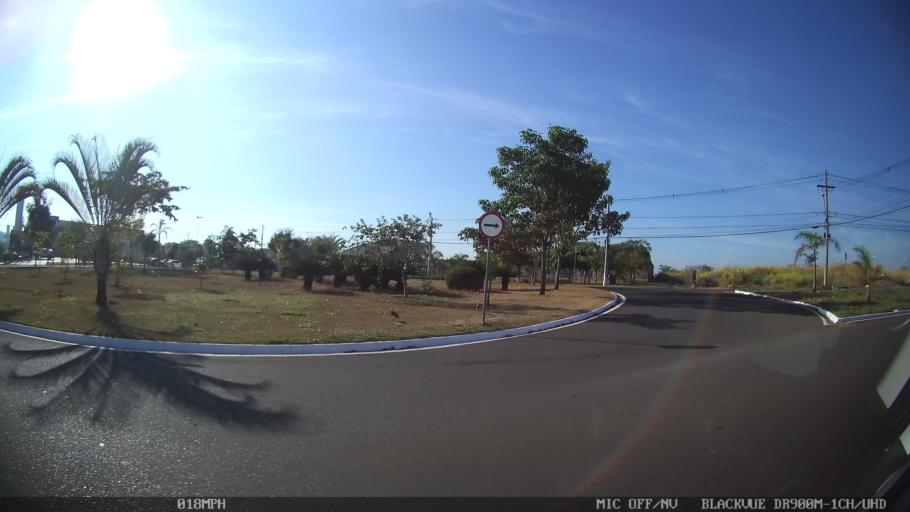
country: BR
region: Sao Paulo
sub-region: Sao Jose Do Rio Preto
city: Sao Jose do Rio Preto
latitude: -20.7733
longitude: -49.3333
